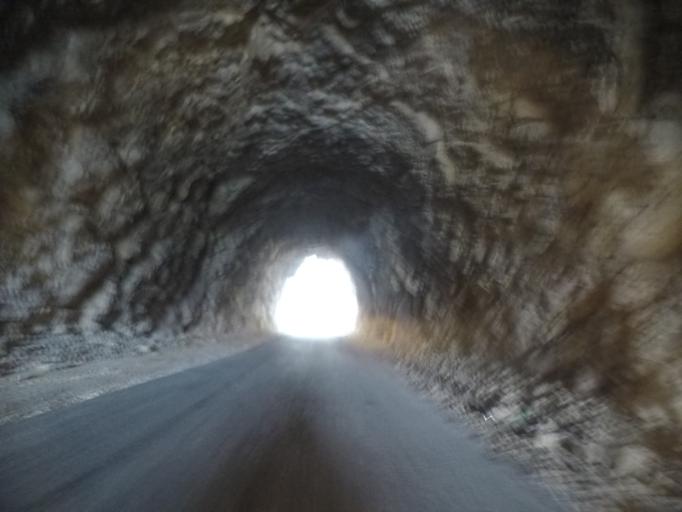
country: ME
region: Opstina Pluzine
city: Pluzine
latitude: 43.1696
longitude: 18.8592
